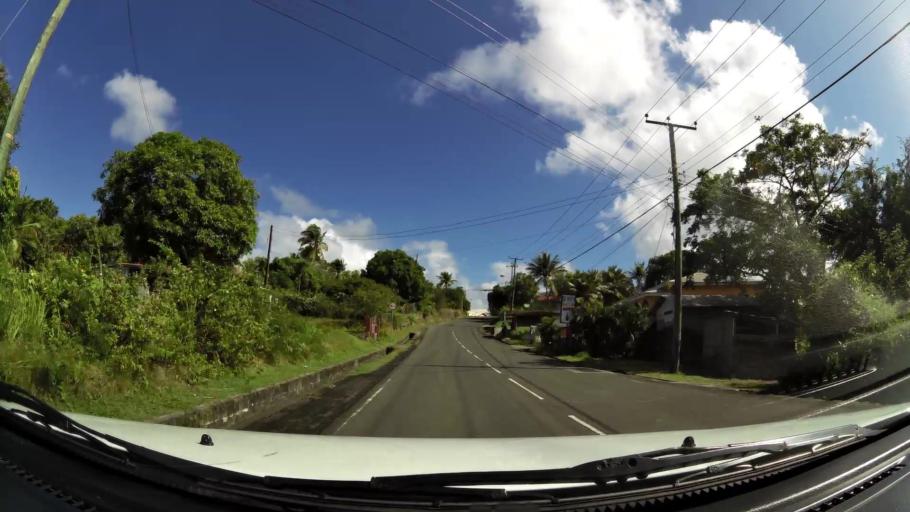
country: LC
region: Choiseul Quarter
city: Choiseul
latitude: 13.7738
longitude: -61.0400
